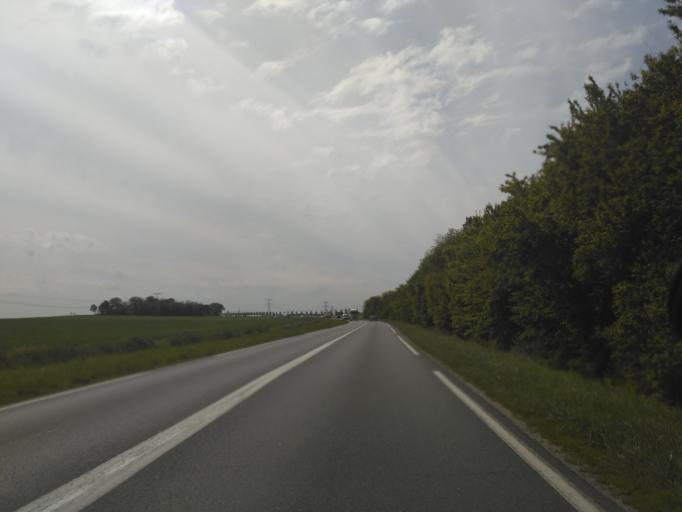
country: FR
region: Ile-de-France
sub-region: Departement de Seine-et-Marne
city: Ozouer-le-Voulgis
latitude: 48.6359
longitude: 2.7660
